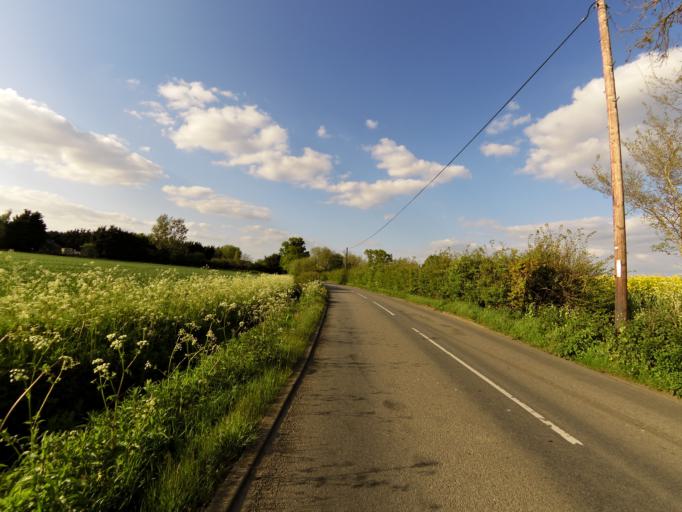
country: GB
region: England
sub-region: Suffolk
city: Halesworth
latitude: 52.3997
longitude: 1.5206
